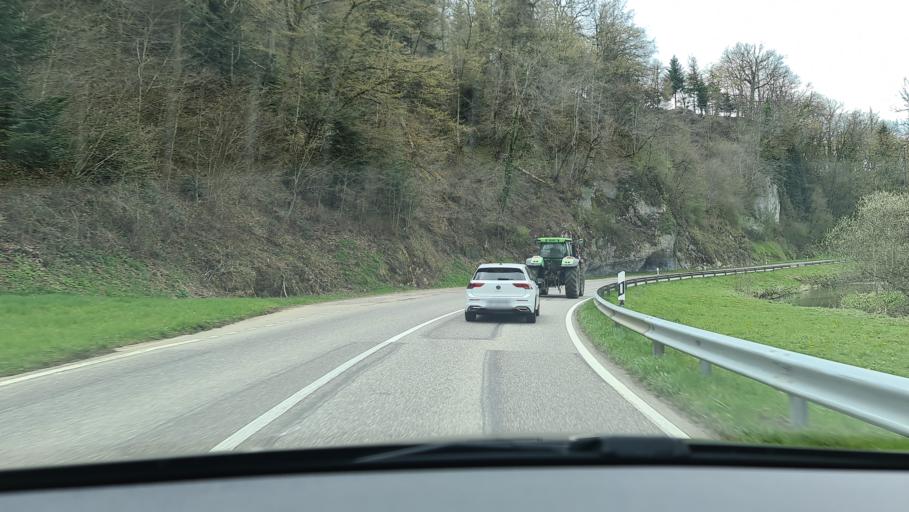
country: CH
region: Jura
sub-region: Porrentruy District
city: Porrentruy
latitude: 47.4319
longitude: 7.0611
